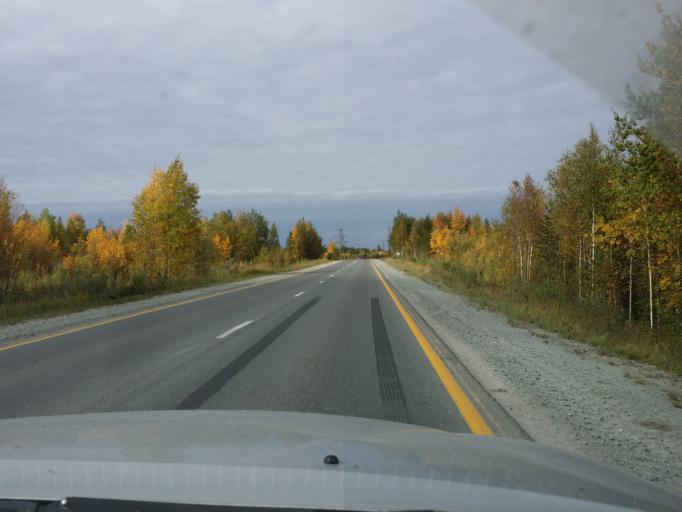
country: RU
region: Khanty-Mansiyskiy Avtonomnyy Okrug
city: Megion
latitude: 61.1019
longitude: 75.9830
